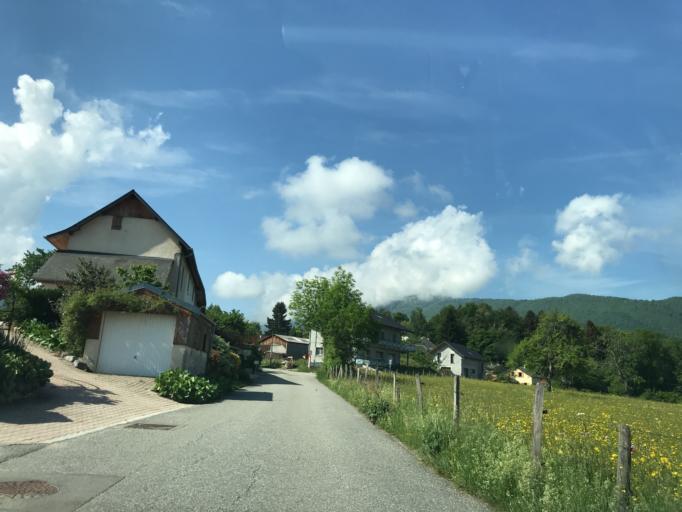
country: FR
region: Rhone-Alpes
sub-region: Departement de la Savoie
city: Vimines
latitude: 45.5510
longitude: 5.8713
